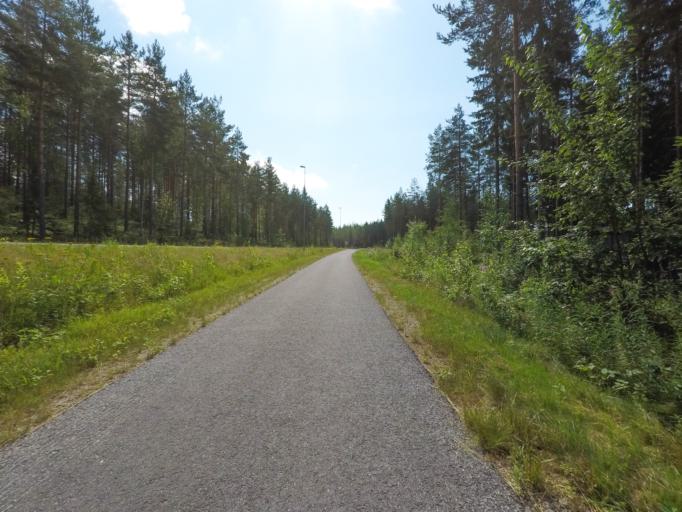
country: FI
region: Southern Savonia
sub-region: Mikkeli
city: Puumala
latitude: 61.5120
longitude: 28.1647
